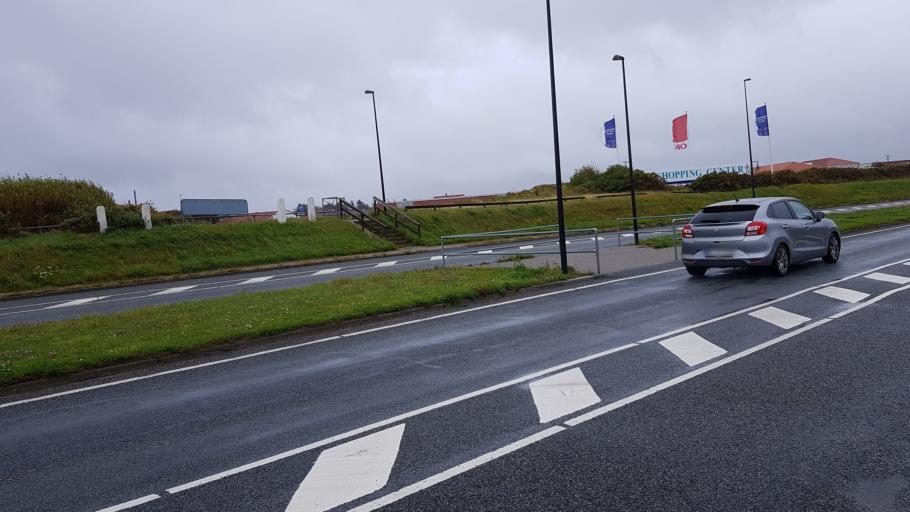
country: DK
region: North Denmark
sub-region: Thisted Kommune
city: Hanstholm
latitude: 57.1149
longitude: 8.6035
